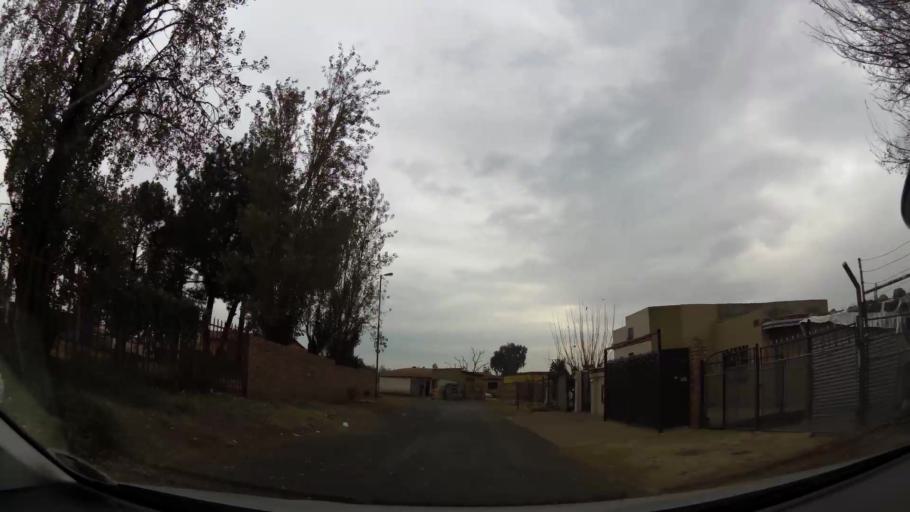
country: ZA
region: Gauteng
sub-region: City of Johannesburg Metropolitan Municipality
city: Soweto
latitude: -26.2540
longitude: 27.8744
